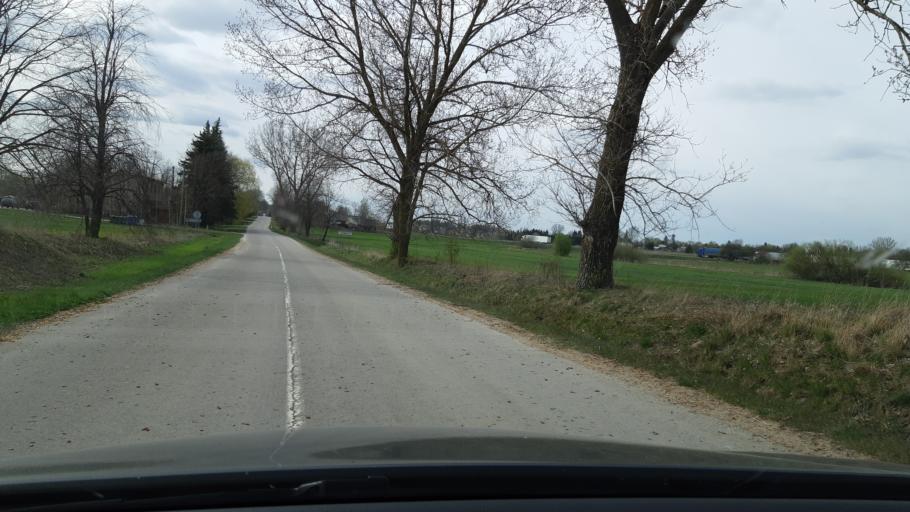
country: LT
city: Virbalis
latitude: 54.6225
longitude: 22.8356
